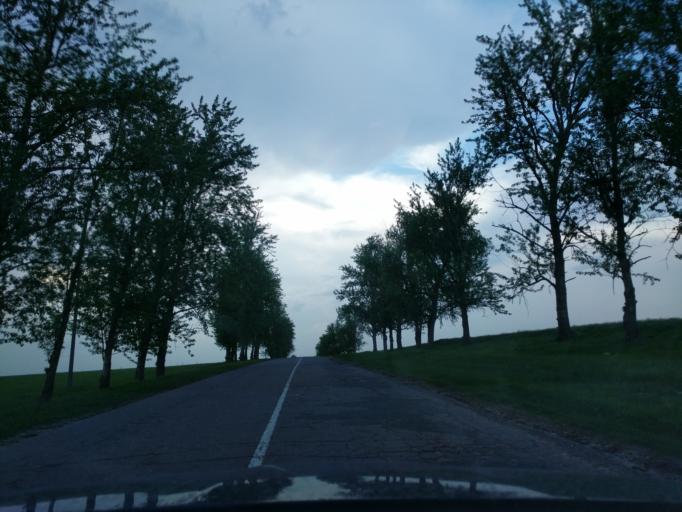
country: BY
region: Minsk
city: Novy Svyerzhan'
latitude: 53.4759
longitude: 26.6323
